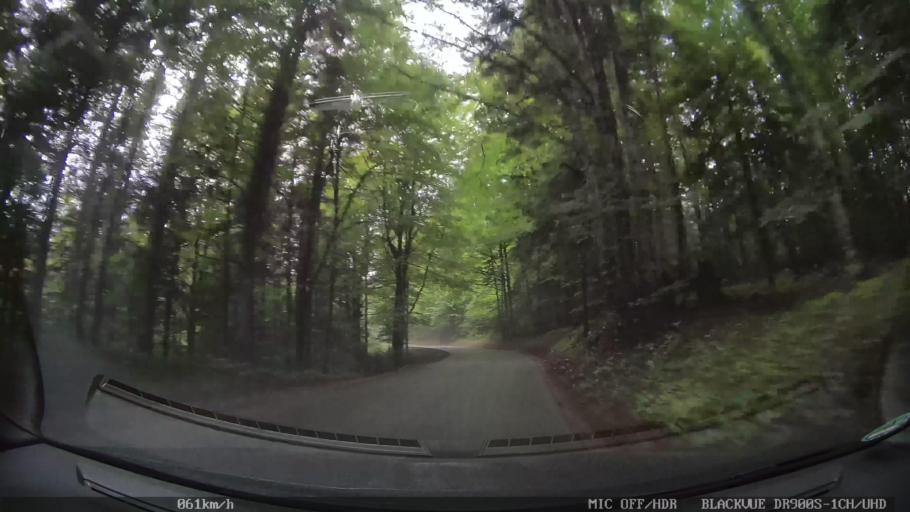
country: HR
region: Licko-Senjska
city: Jezerce
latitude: 44.9379
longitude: 15.5454
